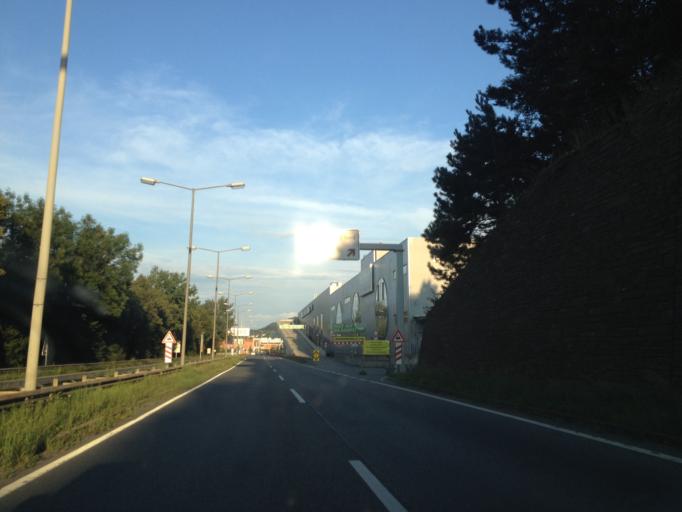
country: AT
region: Styria
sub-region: Graz Stadt
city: Goesting
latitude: 47.1062
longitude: 15.3959
